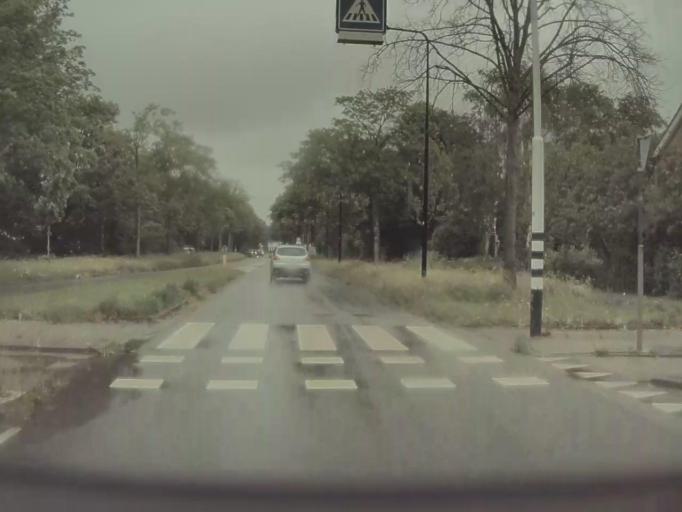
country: NL
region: South Holland
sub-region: Gemeente Voorschoten
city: Voorschoten
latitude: 52.1397
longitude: 4.4611
